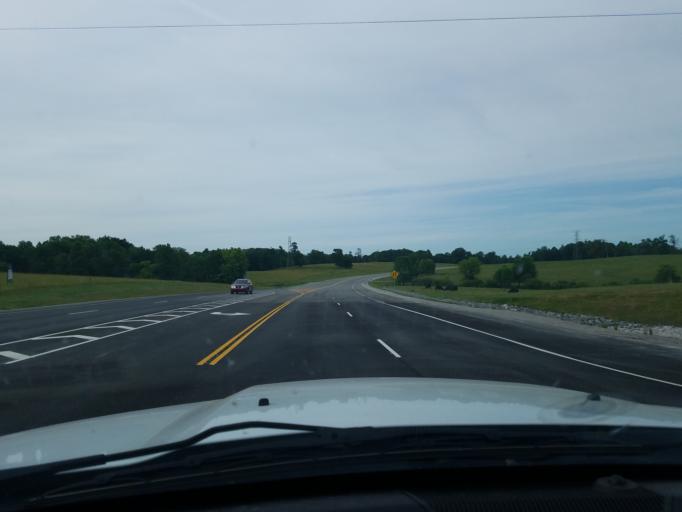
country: US
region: Tennessee
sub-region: Putnam County
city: Baxter
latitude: 36.1430
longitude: -85.5786
